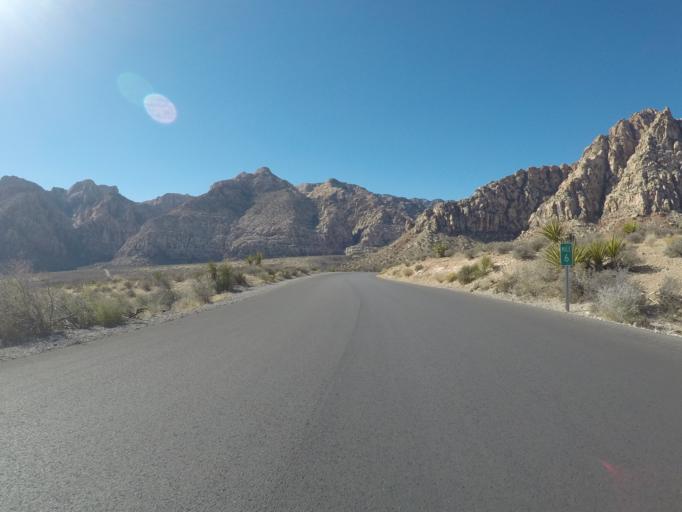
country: US
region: Nevada
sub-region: Clark County
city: Summerlin South
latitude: 36.1629
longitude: -115.4775
